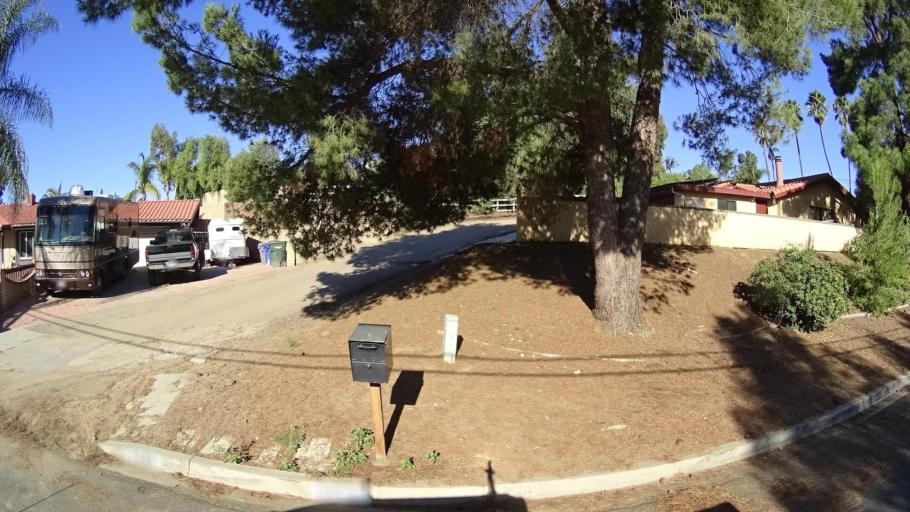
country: US
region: California
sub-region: San Diego County
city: Bonita
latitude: 32.6838
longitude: -117.0166
